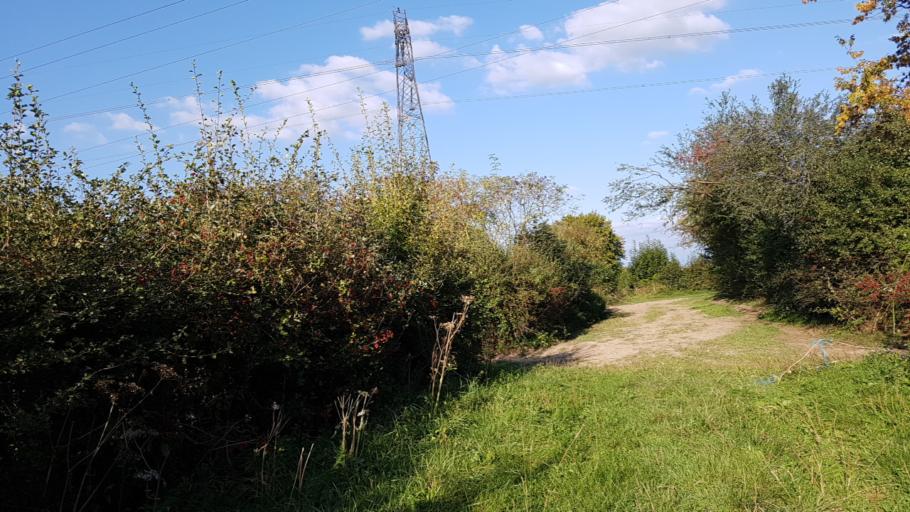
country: FR
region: Picardie
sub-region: Departement de l'Aisne
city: La Capelle
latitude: 49.9811
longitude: 3.9292
